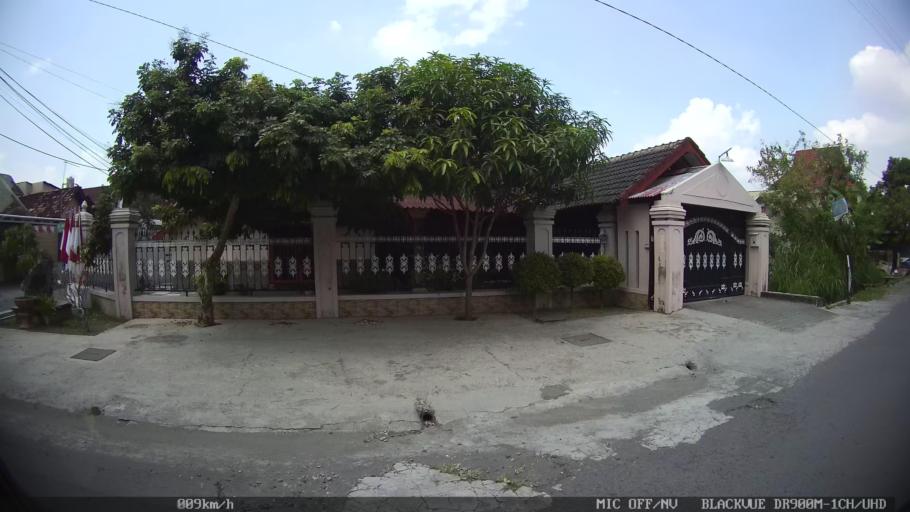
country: ID
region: Daerah Istimewa Yogyakarta
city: Yogyakarta
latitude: -7.8128
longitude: 110.4047
